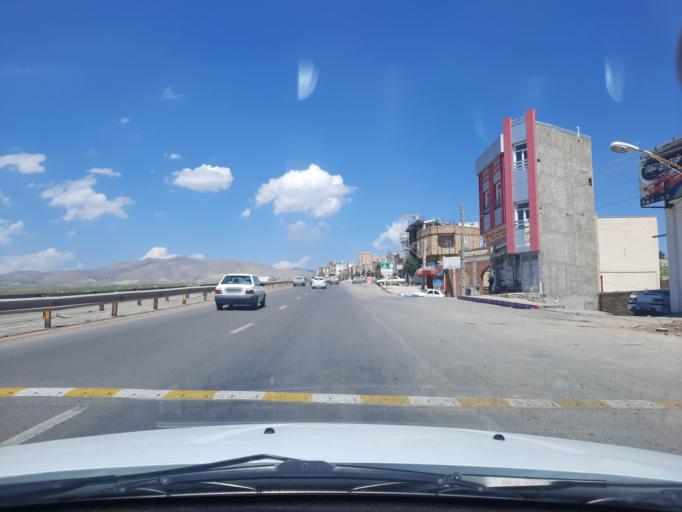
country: IR
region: Qazvin
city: Alvand
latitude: 36.2869
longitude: 50.1323
